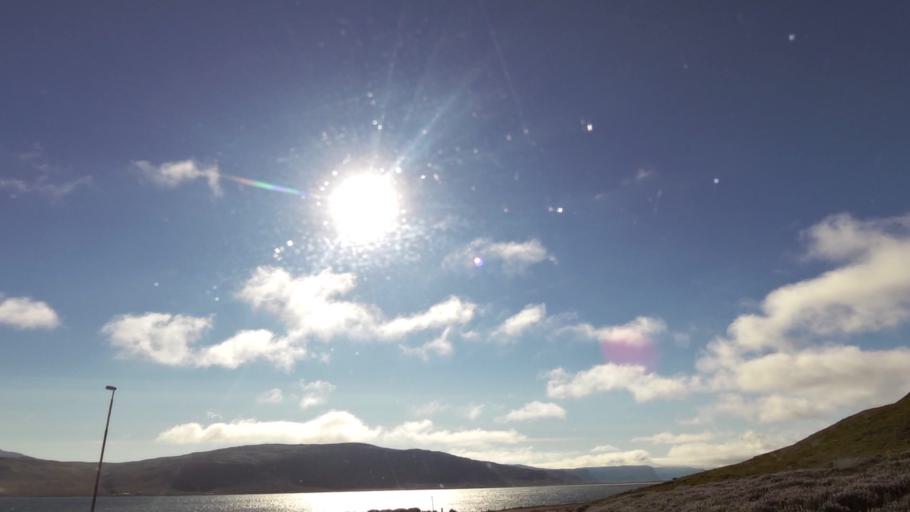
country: IS
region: West
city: Olafsvik
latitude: 65.5435
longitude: -23.8785
